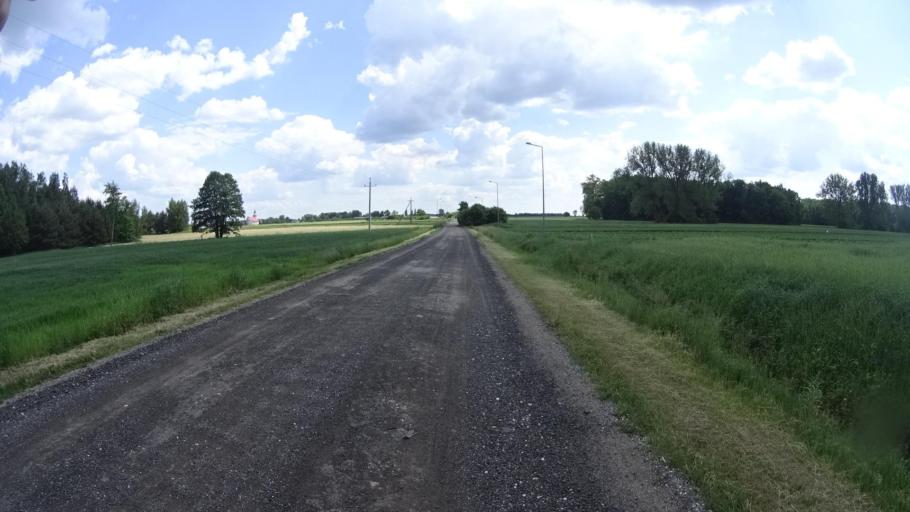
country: PL
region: Masovian Voivodeship
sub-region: Powiat pruszkowski
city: Nadarzyn
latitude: 52.0610
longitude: 20.8220
